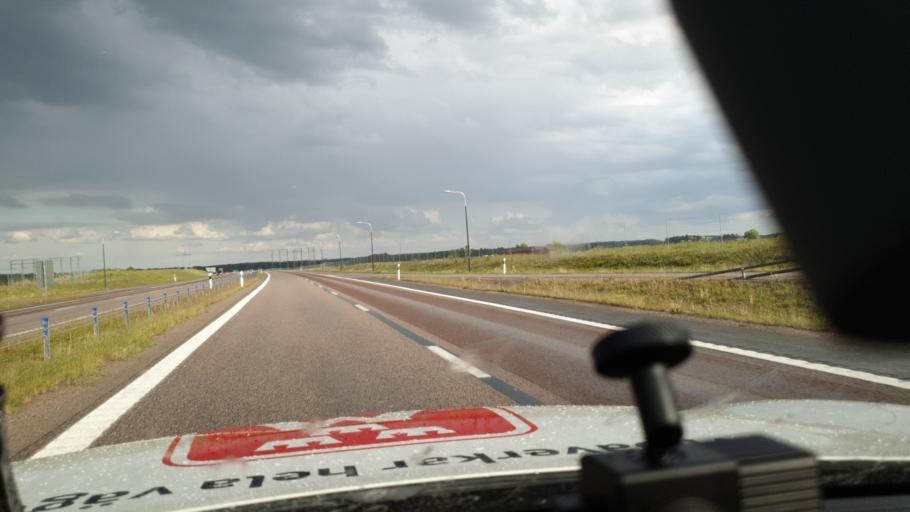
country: SE
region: Uppsala
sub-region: Tierps Kommun
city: Tierp
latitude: 60.3387
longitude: 17.4874
